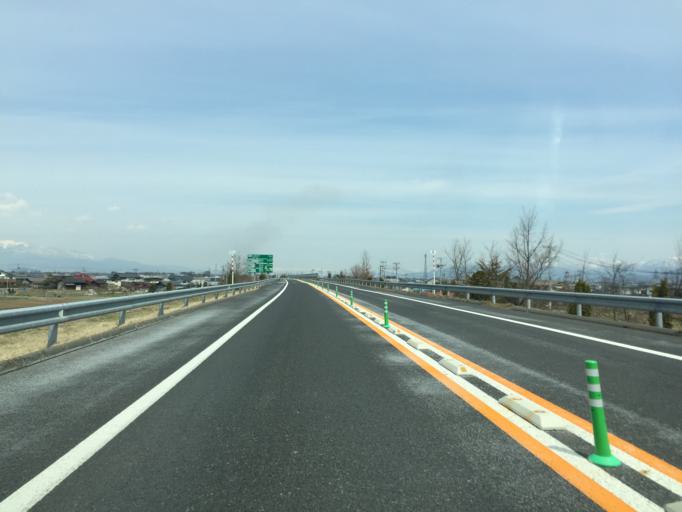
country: JP
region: Yamagata
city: Yamagata-shi
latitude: 38.2809
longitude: 140.2976
